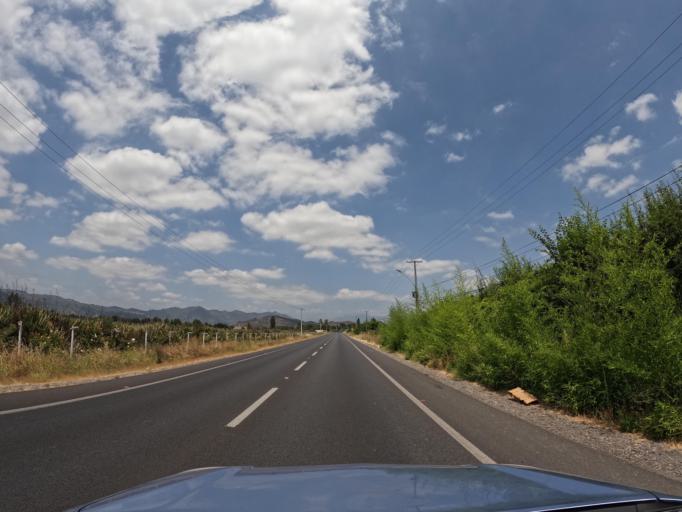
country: CL
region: Maule
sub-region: Provincia de Curico
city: Curico
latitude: -35.0250
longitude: -71.1994
